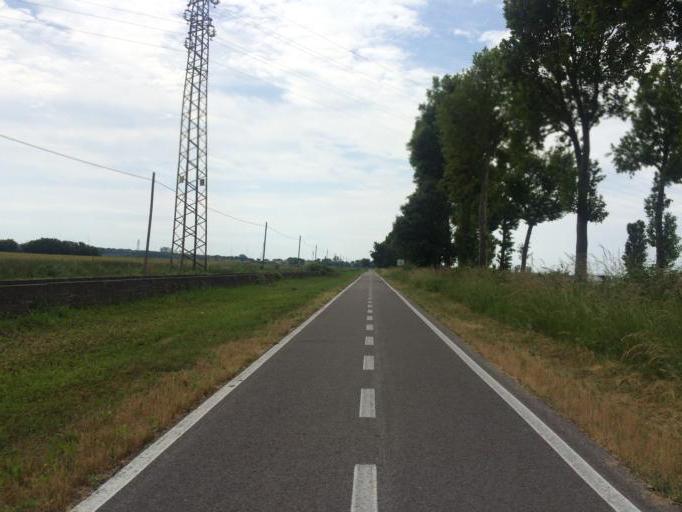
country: IT
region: Friuli Venezia Giulia
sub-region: Provincia di Udine
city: Aquileia
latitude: 45.7402
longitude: 13.3845
